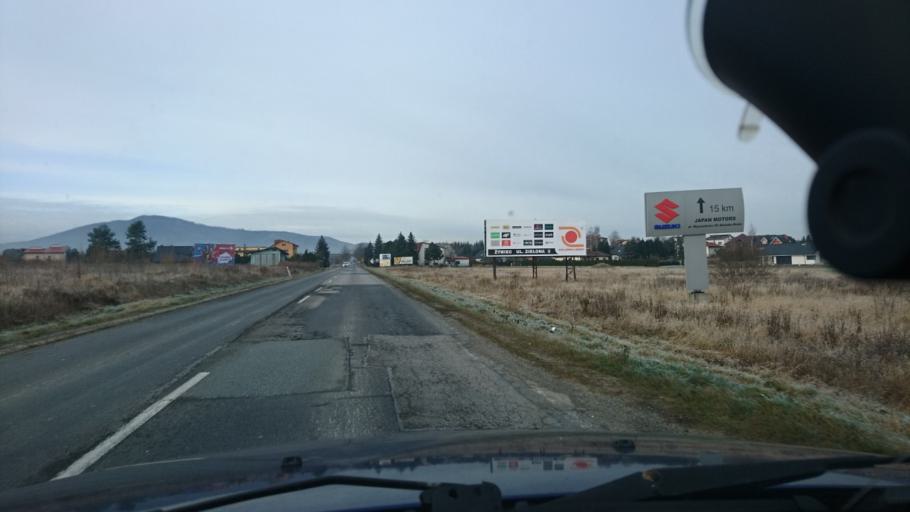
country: PL
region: Silesian Voivodeship
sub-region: Powiat zywiecki
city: Lodygowice
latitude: 49.7307
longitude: 19.1269
